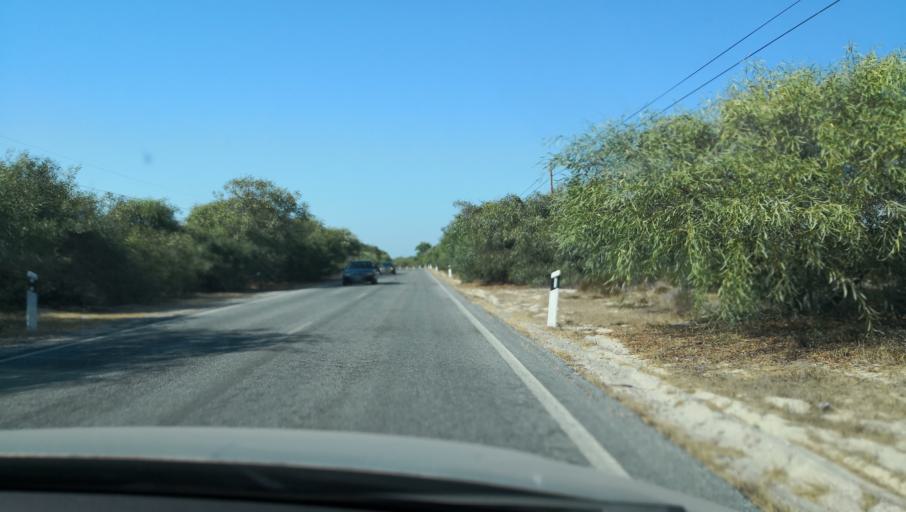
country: PT
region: Setubal
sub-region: Setubal
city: Setubal
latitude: 38.4001
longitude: -8.8063
